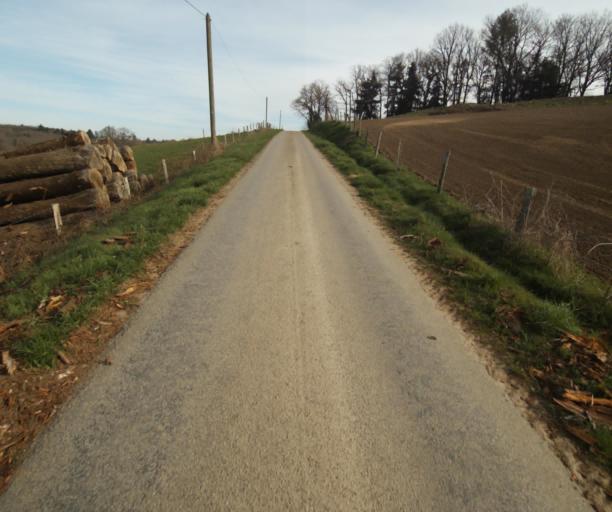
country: FR
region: Limousin
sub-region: Departement de la Correze
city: Chamboulive
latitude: 45.4389
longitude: 1.7446
